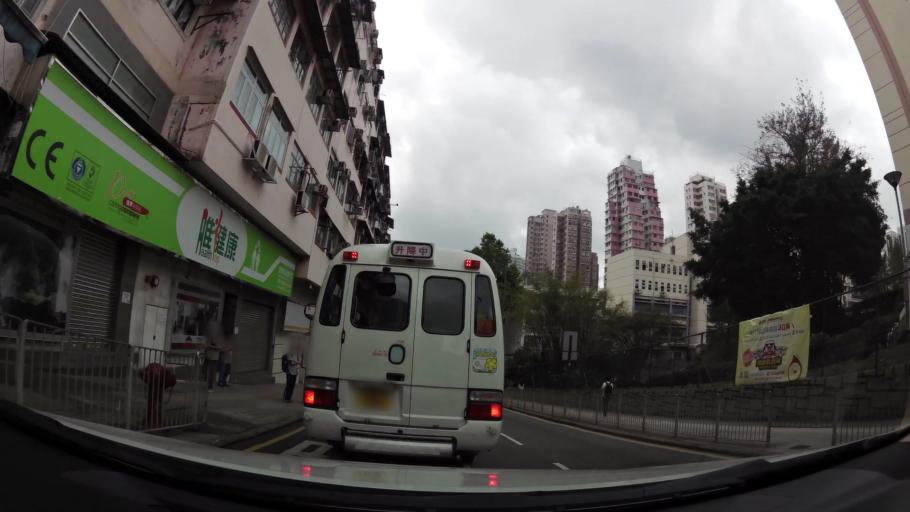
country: HK
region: Wong Tai Sin
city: Wong Tai Sin
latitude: 22.3456
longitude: 114.1975
